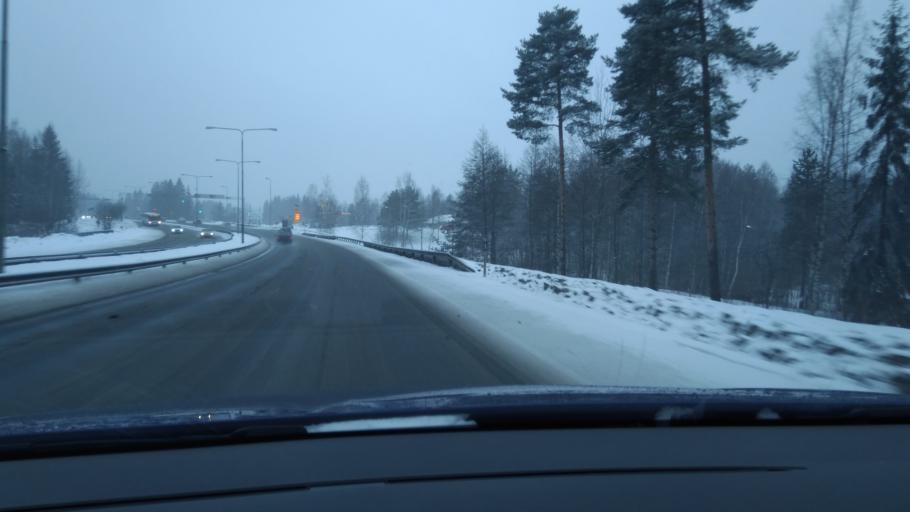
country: FI
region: Pirkanmaa
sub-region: Tampere
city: Tampere
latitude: 61.5028
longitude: 23.8647
